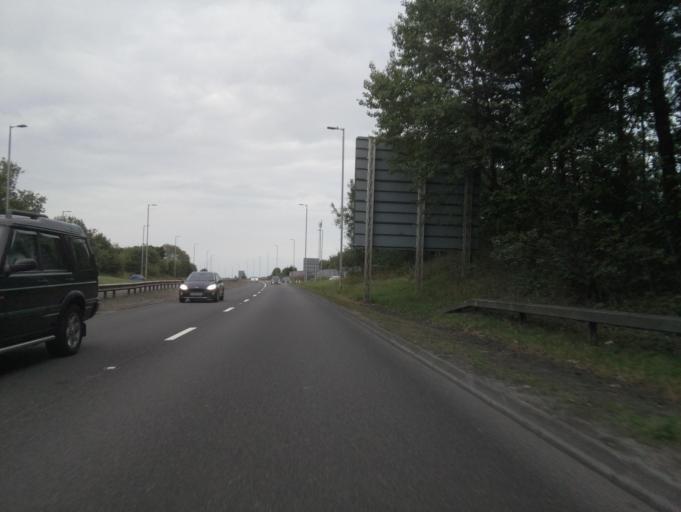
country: GB
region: Scotland
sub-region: North Lanarkshire
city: Bellshill
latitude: 55.8197
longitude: -4.0398
